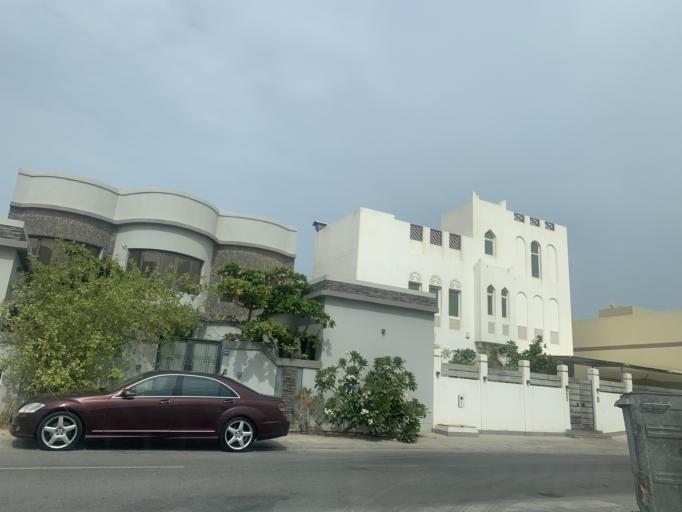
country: BH
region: Muharraq
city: Al Muharraq
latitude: 26.2856
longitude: 50.6360
